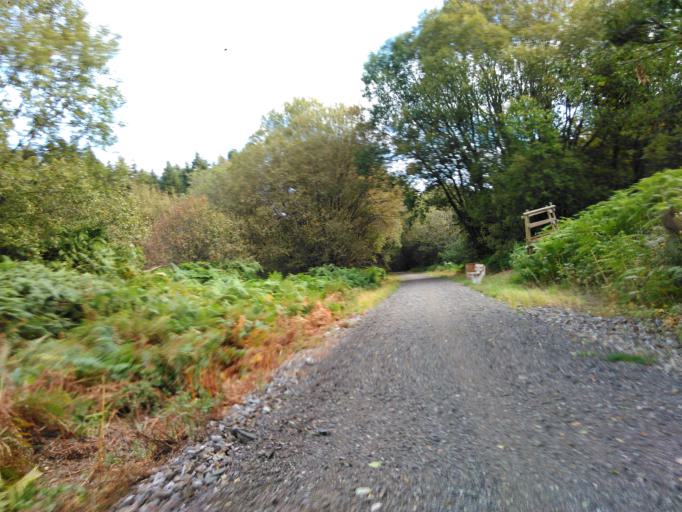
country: BE
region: Wallonia
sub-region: Province du Luxembourg
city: Vaux-sur-Sure
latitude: 49.9098
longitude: 5.4954
